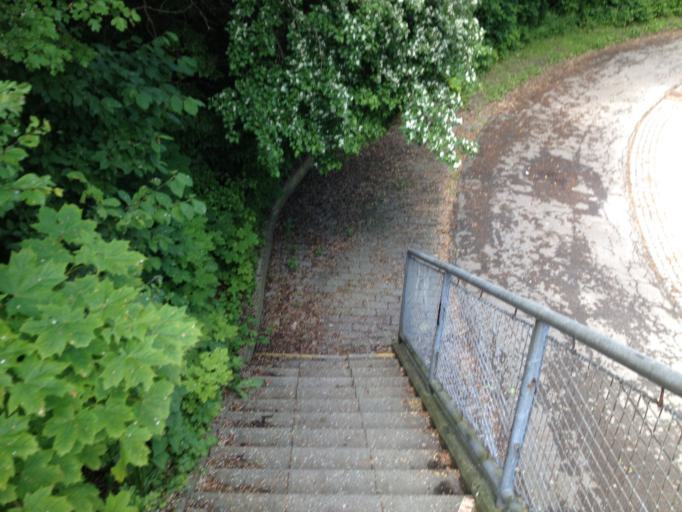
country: DK
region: Capital Region
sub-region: Fredensborg Kommune
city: Niva
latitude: 55.9376
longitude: 12.4990
